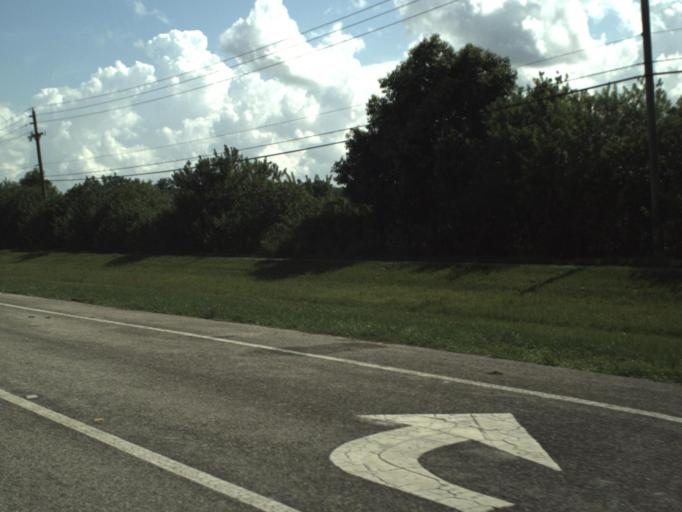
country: US
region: Florida
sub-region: Palm Beach County
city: Villages of Oriole
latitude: 26.5211
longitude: -80.2055
